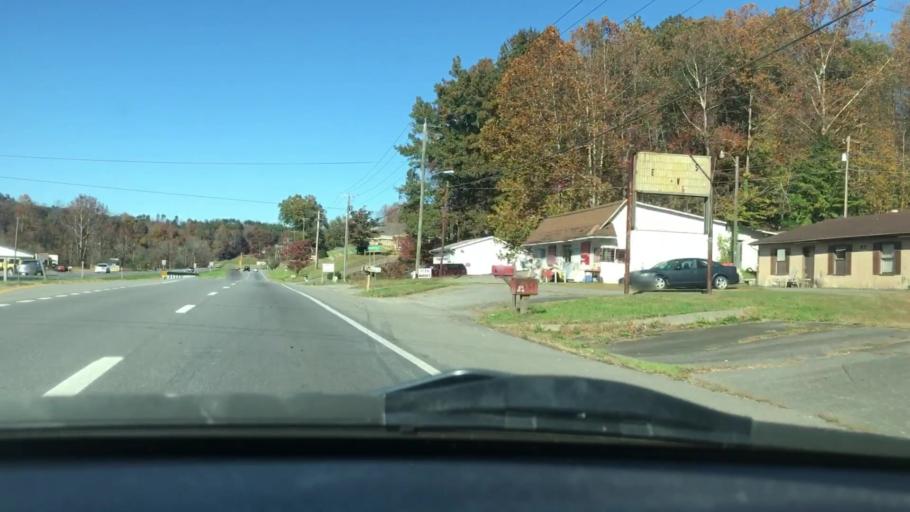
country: US
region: Virginia
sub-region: Henry County
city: Stanleytown
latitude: 36.7538
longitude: -79.9380
